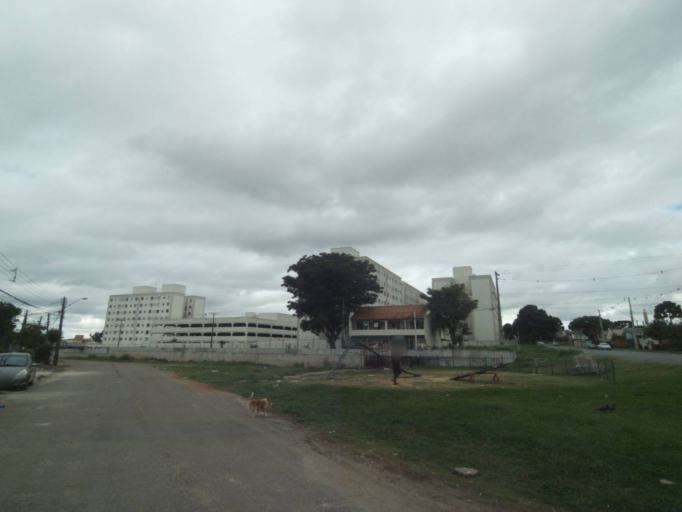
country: BR
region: Parana
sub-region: Curitiba
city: Curitiba
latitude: -25.4798
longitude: -49.2732
